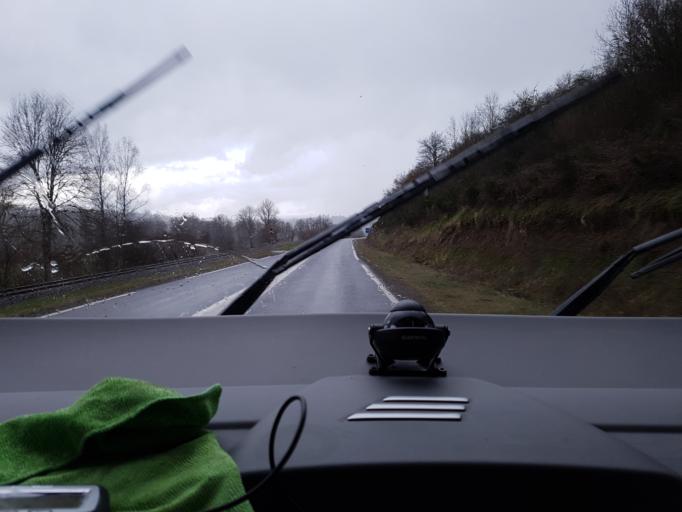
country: FR
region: Auvergne
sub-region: Departement du Puy-de-Dome
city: Gelles
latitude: 45.7766
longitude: 2.8320
